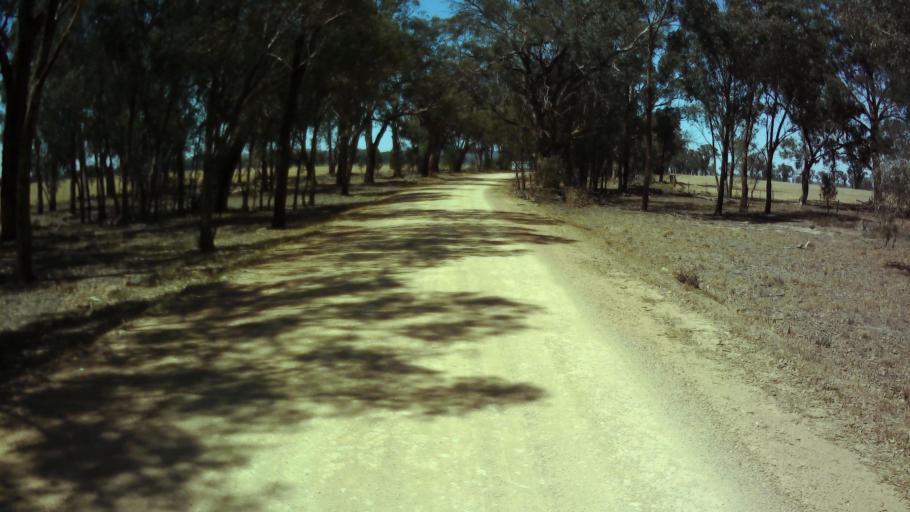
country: AU
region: New South Wales
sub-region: Weddin
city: Grenfell
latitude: -34.0333
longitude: 148.0138
